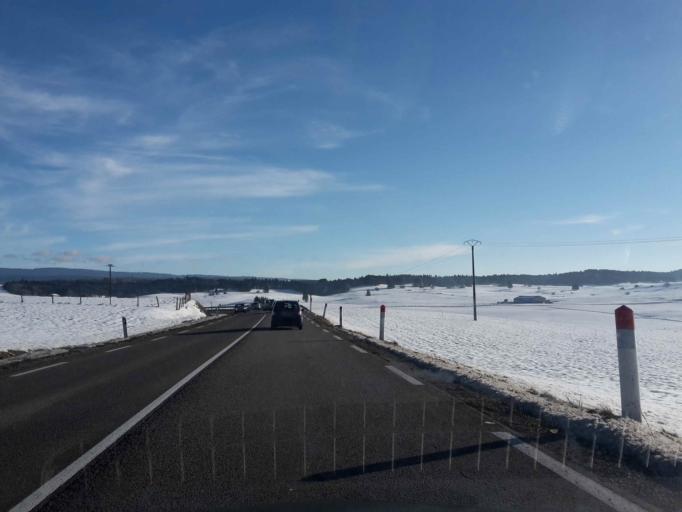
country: FR
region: Franche-Comte
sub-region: Departement du Doubs
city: Doubs
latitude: 46.9846
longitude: 6.3311
